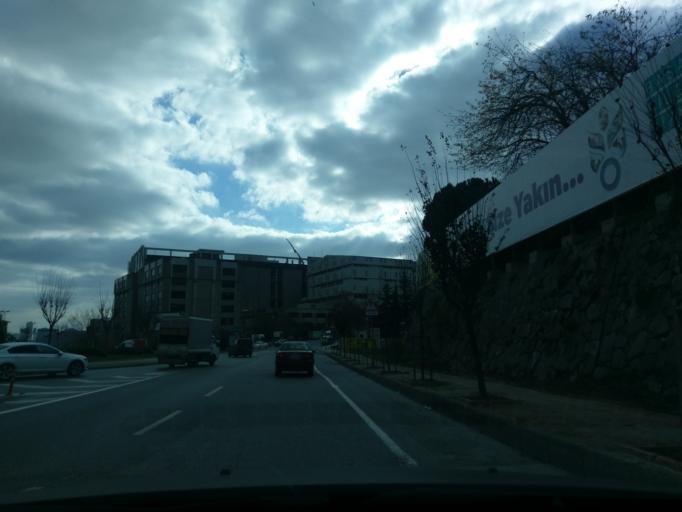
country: TR
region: Istanbul
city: Basaksehir
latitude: 41.0912
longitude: 28.8024
